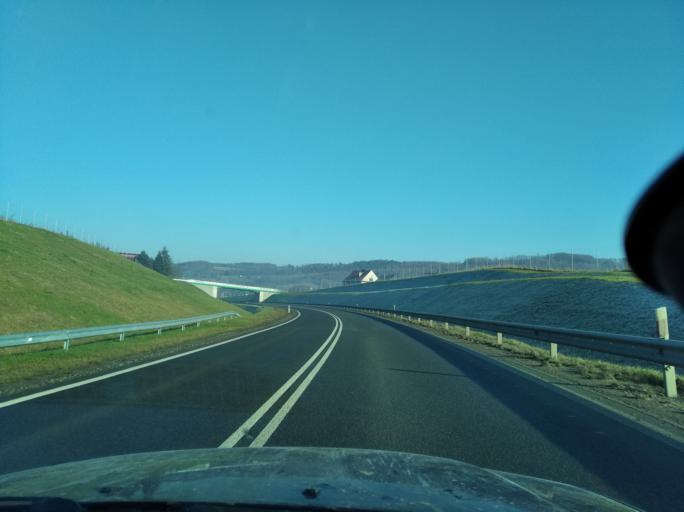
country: PL
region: Subcarpathian Voivodeship
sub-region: Powiat strzyzowski
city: Strzyzow
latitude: 49.8637
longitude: 21.8193
